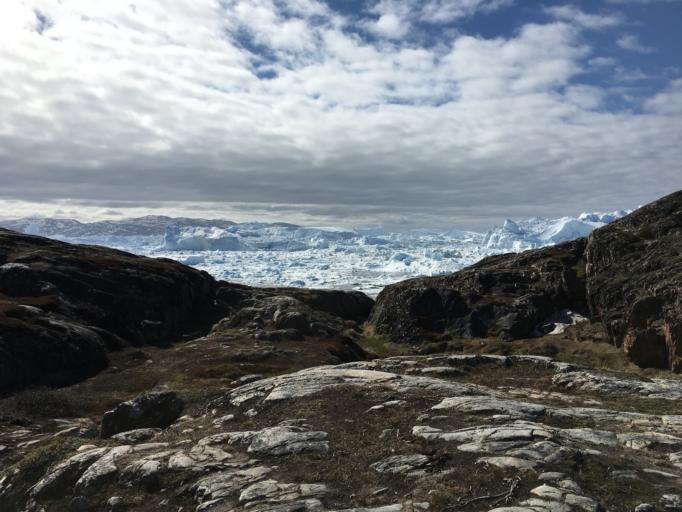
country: GL
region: Qaasuitsup
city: Ilulissat
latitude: 69.2005
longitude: -51.1262
